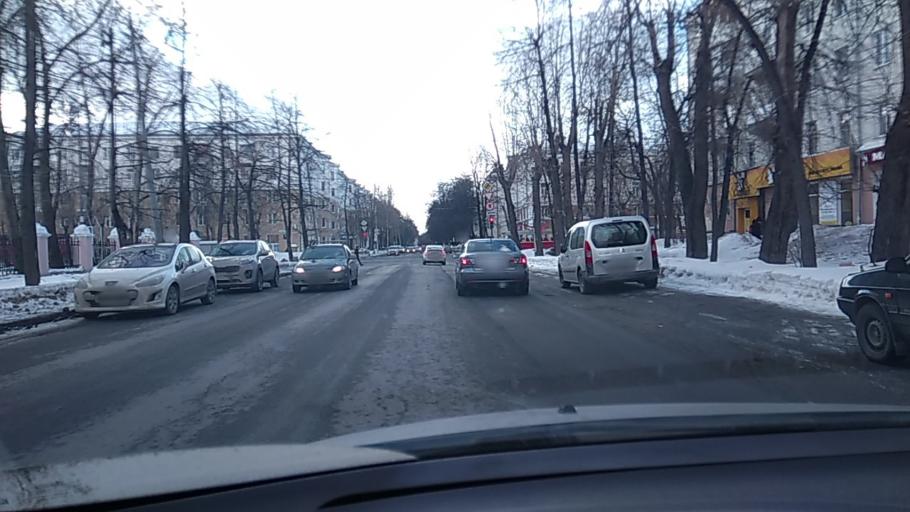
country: RU
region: Sverdlovsk
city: Yekaterinburg
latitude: 56.8458
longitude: 60.6458
